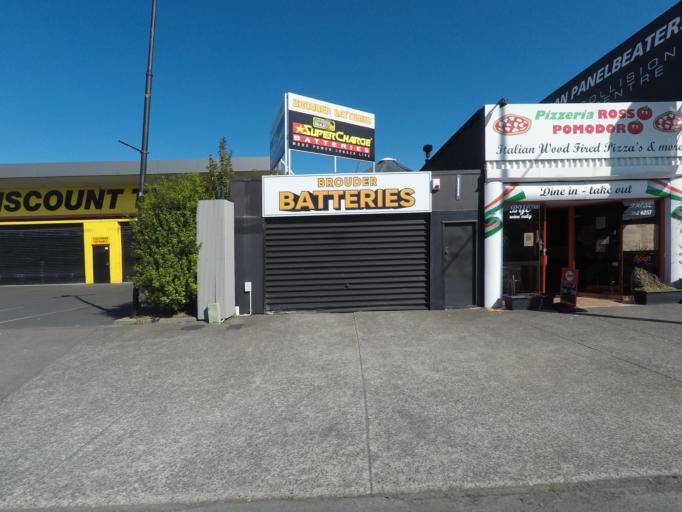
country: NZ
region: Auckland
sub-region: Auckland
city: Auckland
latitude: -36.8658
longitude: 174.7434
